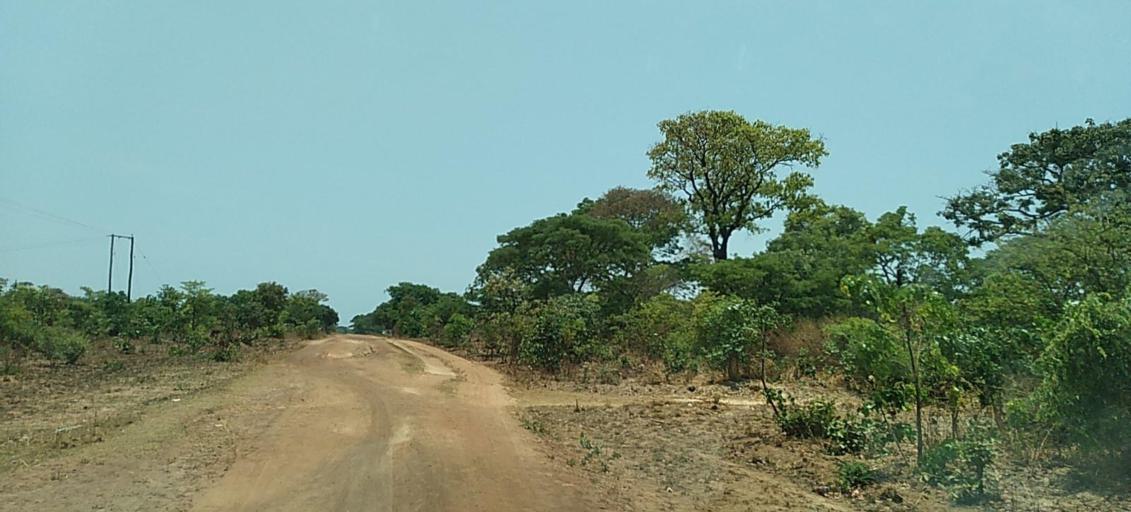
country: ZM
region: Copperbelt
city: Mpongwe
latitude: -13.7929
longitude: 27.8625
